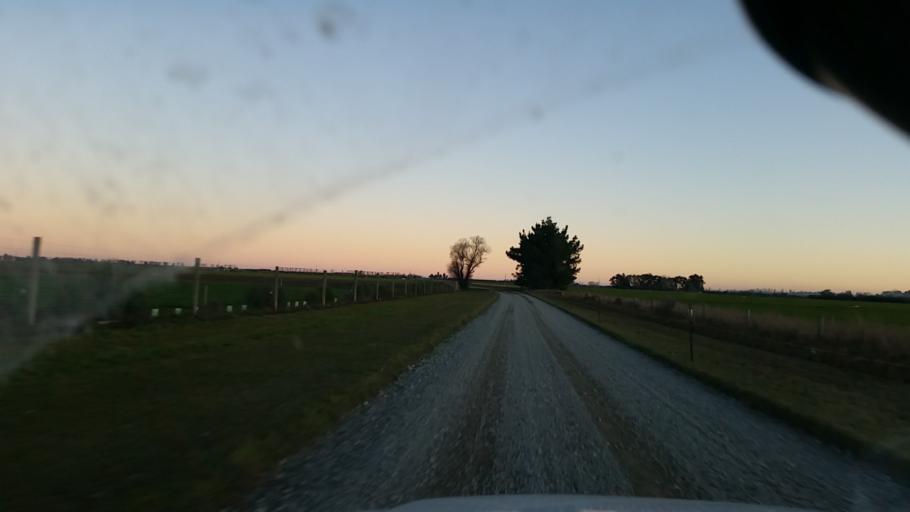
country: NZ
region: Canterbury
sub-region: Ashburton District
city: Tinwald
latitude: -44.0603
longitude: 171.6609
